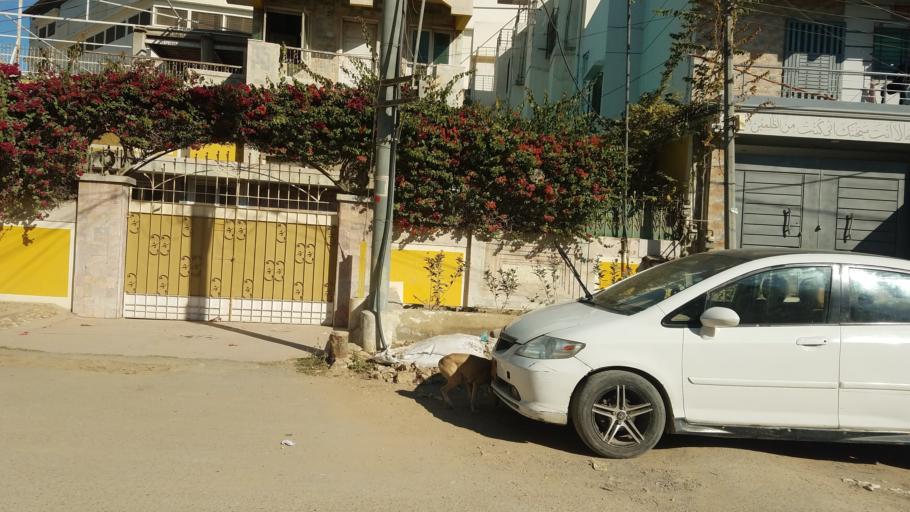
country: PK
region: Sindh
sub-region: Karachi District
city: Karachi
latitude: 24.9273
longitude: 67.0526
